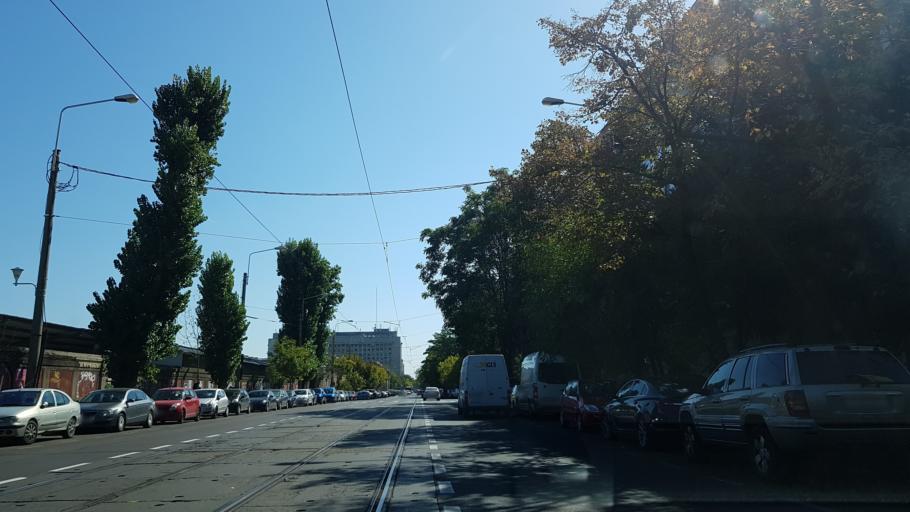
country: RO
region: Bucuresti
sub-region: Municipiul Bucuresti
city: Bucuresti
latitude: 44.4478
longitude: 26.0709
